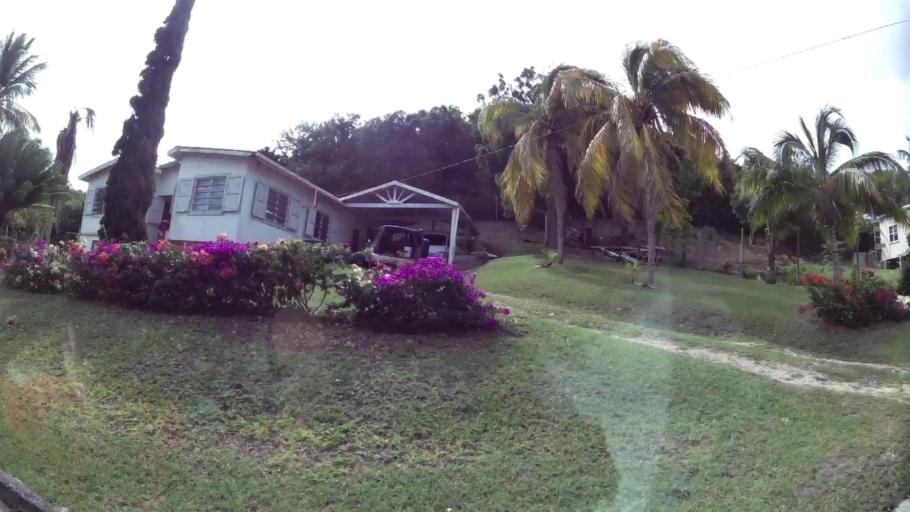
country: AG
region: Saint Peter
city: Parham
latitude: 17.0575
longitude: -61.7287
